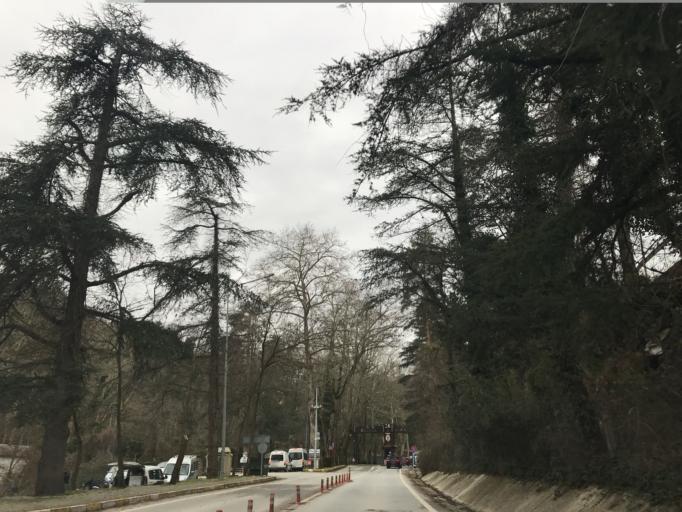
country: TR
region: Yalova
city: Termal
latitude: 40.6022
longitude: 29.1775
